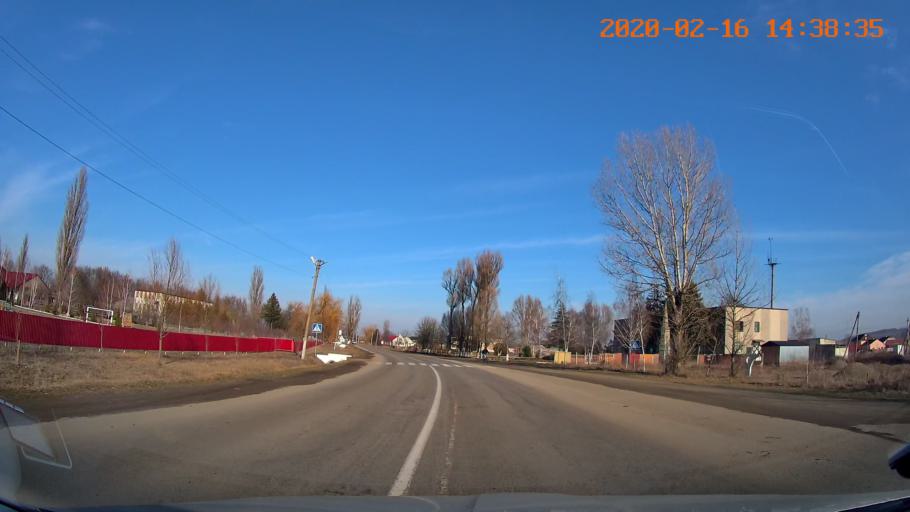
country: RO
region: Botosani
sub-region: Comuna Darabani
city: Bajura
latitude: 48.2330
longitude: 26.5433
